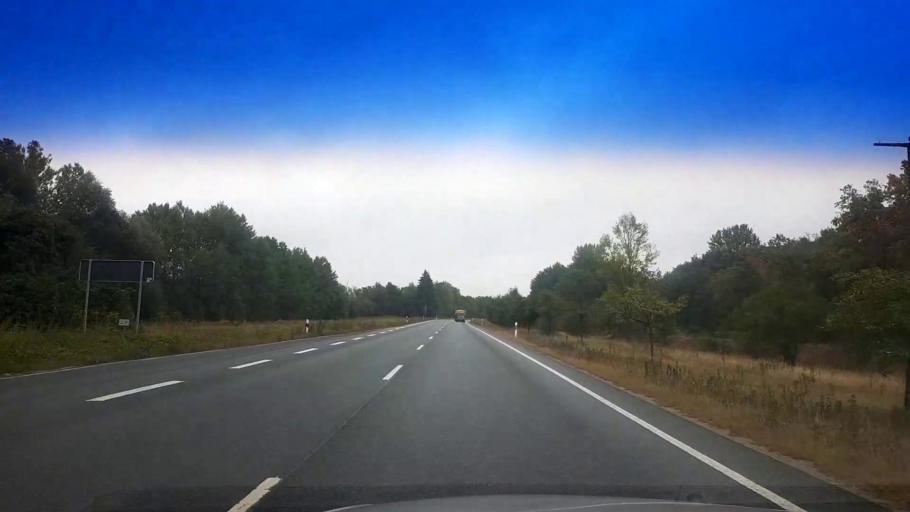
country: DE
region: Bavaria
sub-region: Upper Franconia
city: Eggolsheim
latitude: 49.7468
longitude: 11.0552
